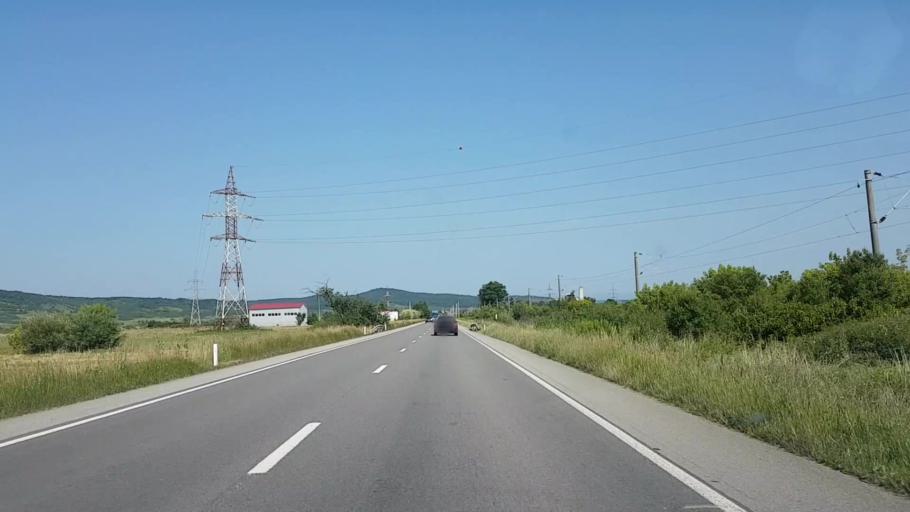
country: RO
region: Bistrita-Nasaud
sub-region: Comuna Sintereag
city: Cociu
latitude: 47.1817
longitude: 24.2529
